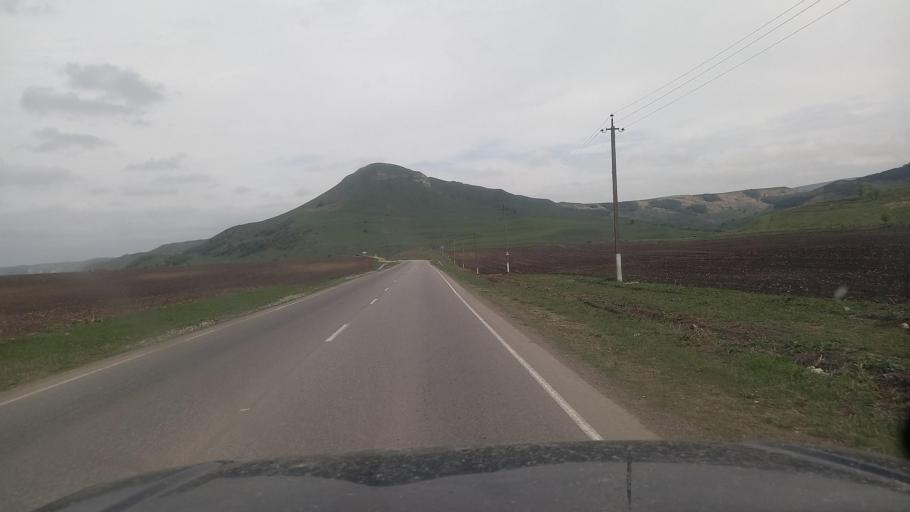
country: RU
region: Kabardino-Balkariya
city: Kamennomostskoye
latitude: 43.7248
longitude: 43.1198
